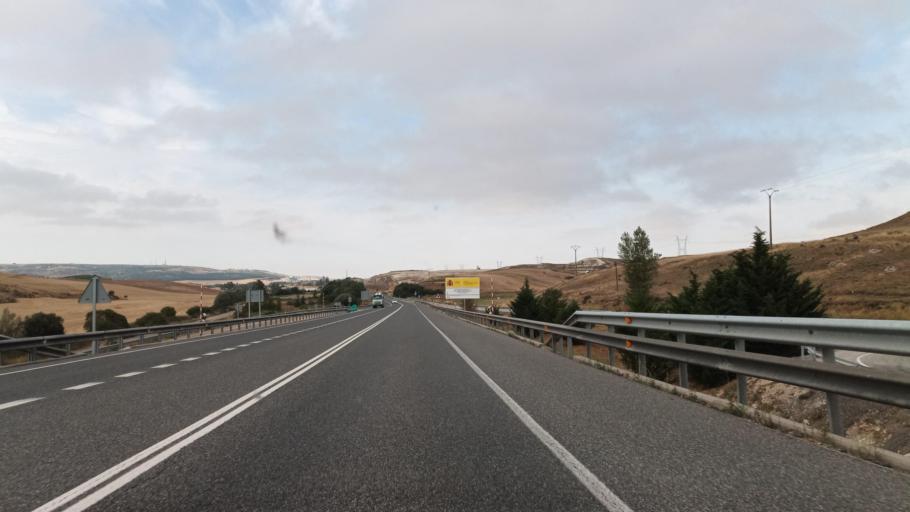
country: ES
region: Castille and Leon
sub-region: Provincia de Burgos
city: Fresno de Rodilla
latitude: 42.4239
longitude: -3.5104
